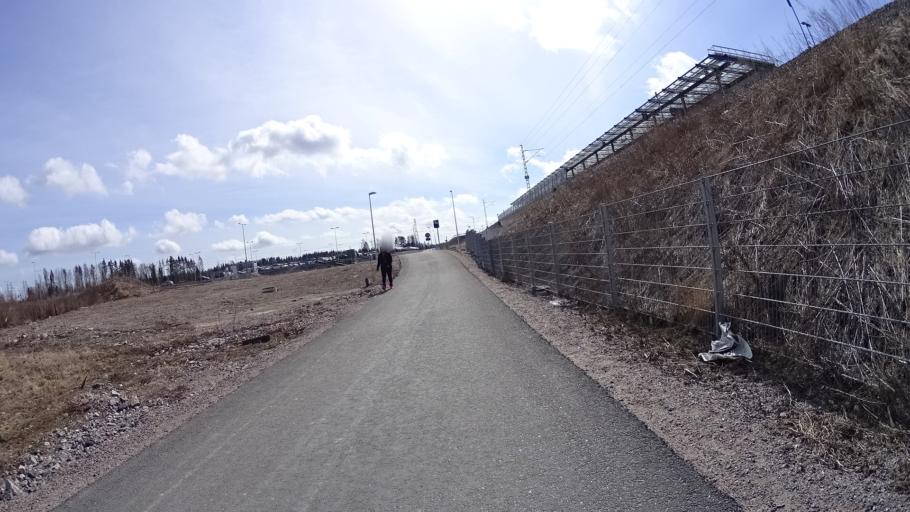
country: FI
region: Uusimaa
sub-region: Helsinki
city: Kilo
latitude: 60.2956
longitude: 24.8441
